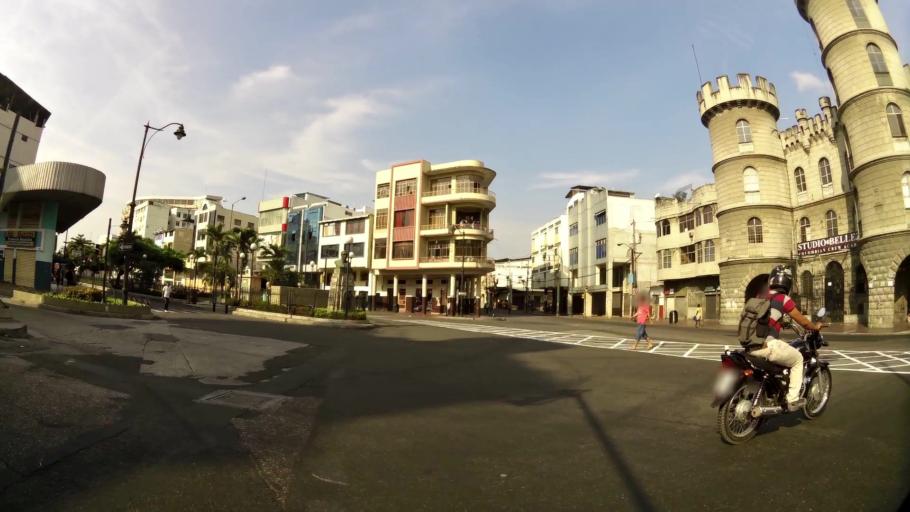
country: EC
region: Guayas
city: Guayaquil
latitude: -2.1961
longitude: -79.8861
